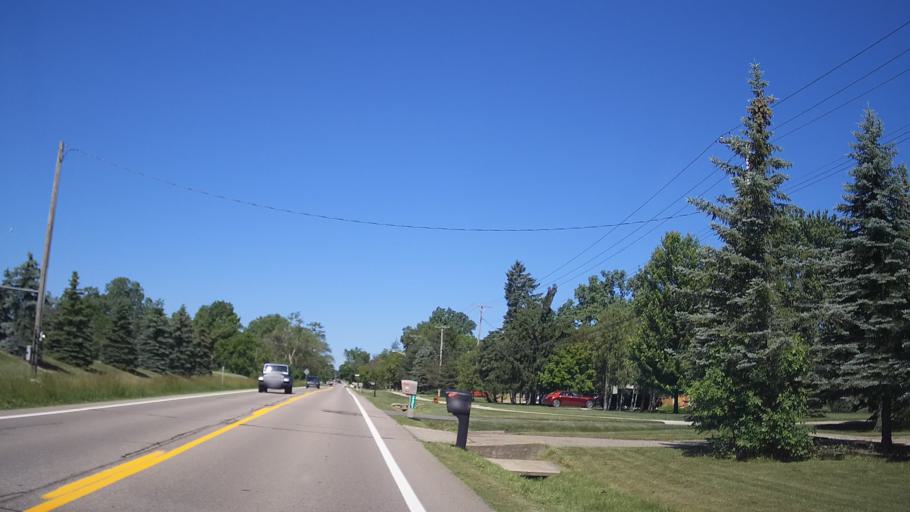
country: US
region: Michigan
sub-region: Oakland County
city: Troy
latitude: 42.6068
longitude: -83.1376
